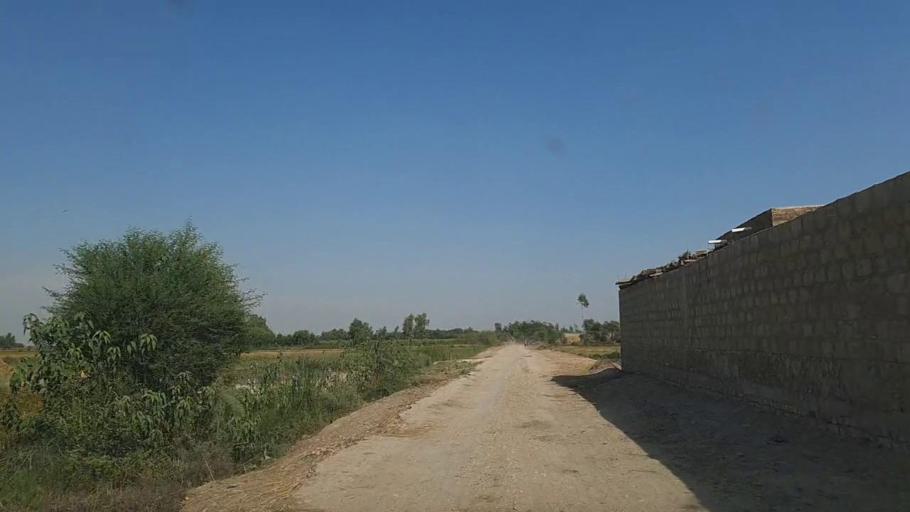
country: PK
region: Sindh
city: Mirpur Batoro
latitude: 24.7978
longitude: 68.2737
